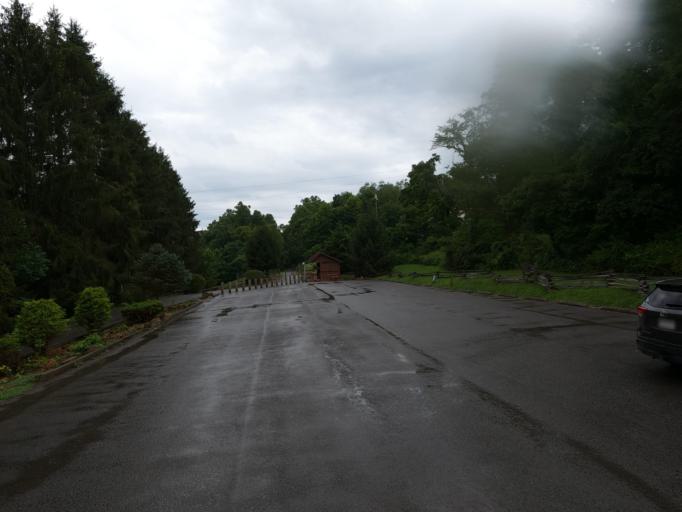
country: US
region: West Virginia
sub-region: Marion County
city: Fairmont
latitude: 39.5177
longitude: -80.0951
